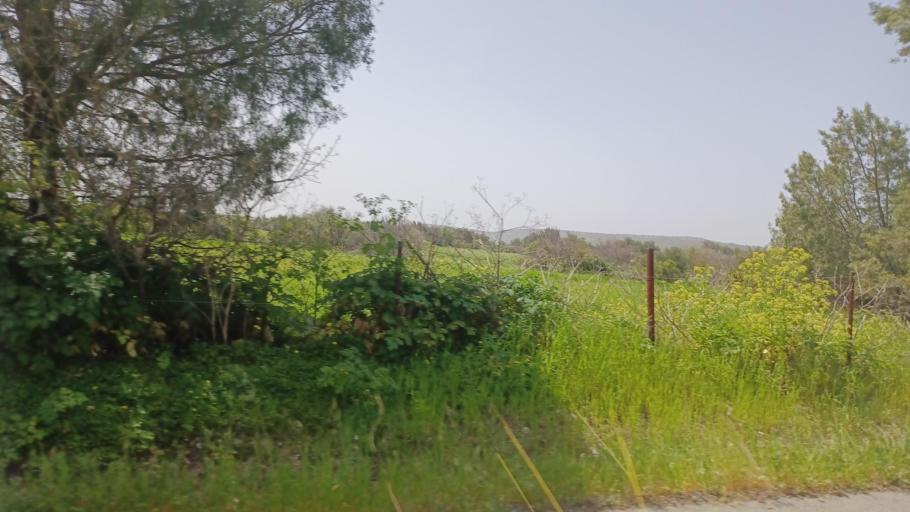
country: CY
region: Limassol
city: Pissouri
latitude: 34.7329
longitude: 32.7367
